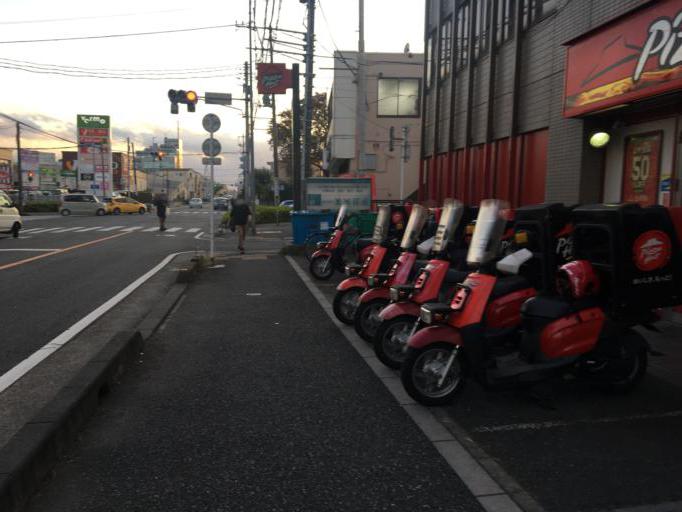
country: JP
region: Saitama
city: Shiki
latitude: 35.8283
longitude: 139.5733
